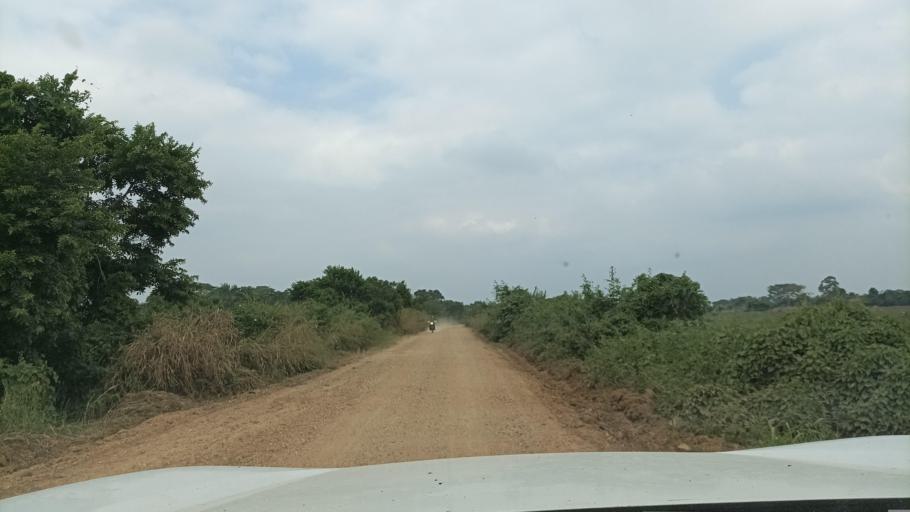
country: MX
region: Veracruz
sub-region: Texistepec
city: San Lorenzo Tenochtitlan
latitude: 17.7804
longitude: -94.7916
